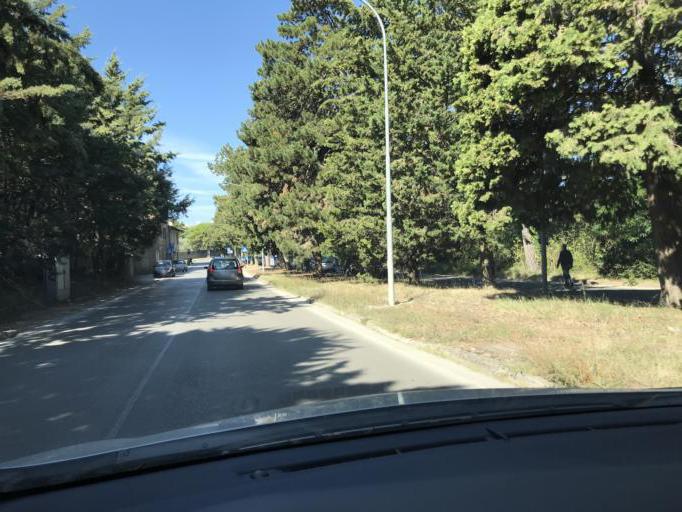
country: IT
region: Umbria
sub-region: Provincia di Perugia
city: Perugia
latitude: 43.1107
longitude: 12.4107
